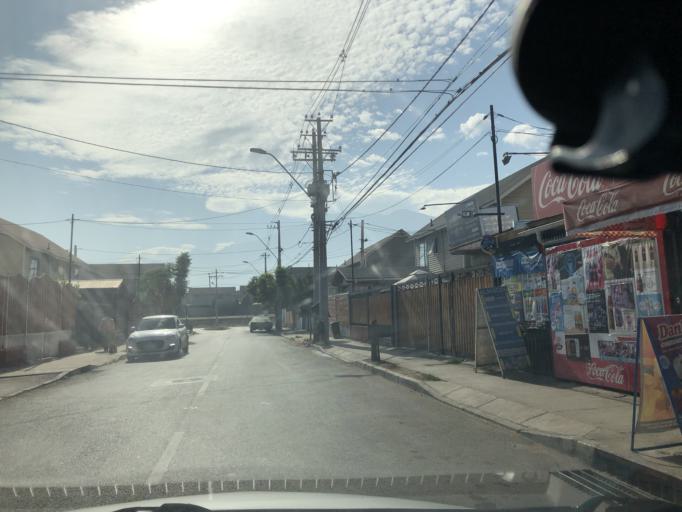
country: CL
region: Santiago Metropolitan
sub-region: Provincia de Cordillera
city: Puente Alto
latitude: -33.5995
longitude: -70.5495
